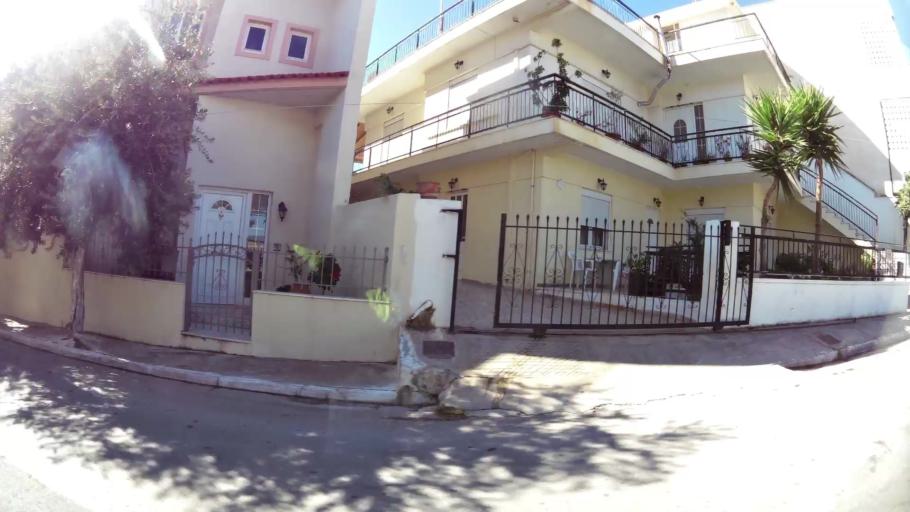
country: GR
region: Attica
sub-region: Nomarchia Anatolikis Attikis
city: Koropi
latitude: 37.9004
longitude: 23.8804
